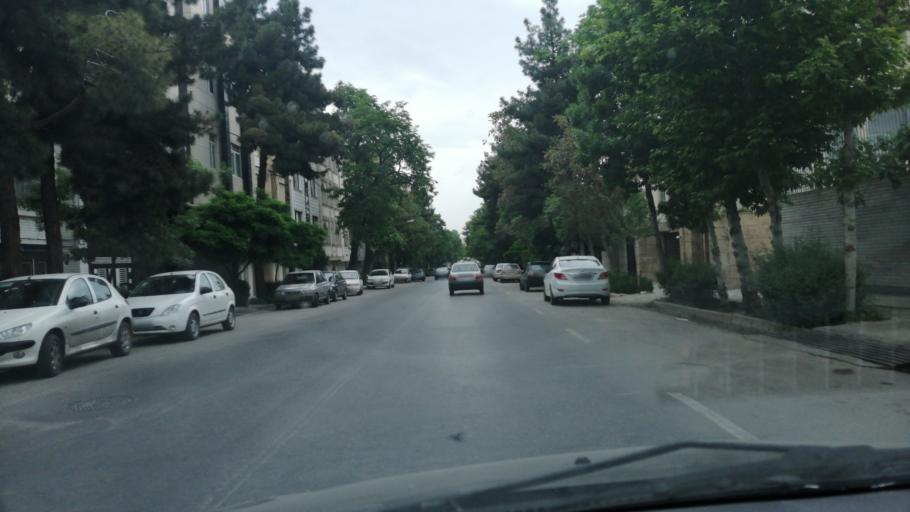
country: IR
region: Razavi Khorasan
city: Mashhad
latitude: 36.2834
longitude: 59.5720
